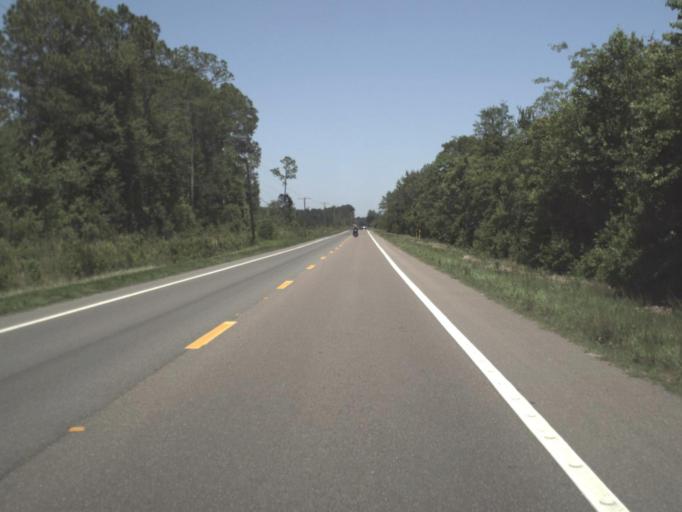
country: US
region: Florida
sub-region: Baker County
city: Macclenny
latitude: 30.2686
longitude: -82.2008
